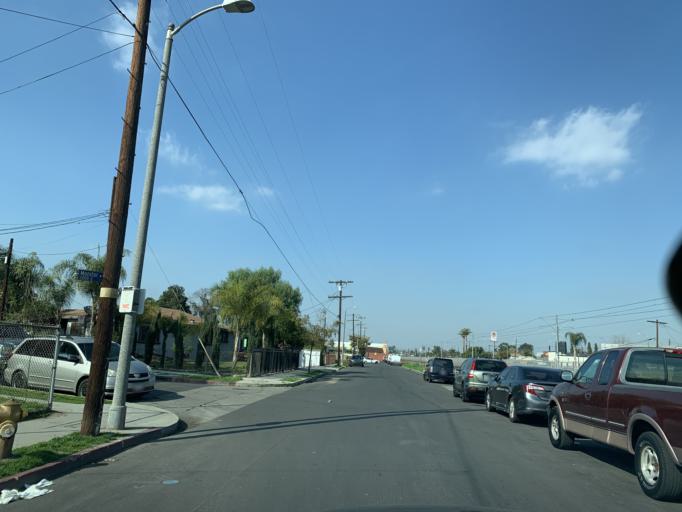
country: US
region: California
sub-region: Los Angeles County
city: Willowbrook
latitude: 33.9329
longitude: -118.2404
